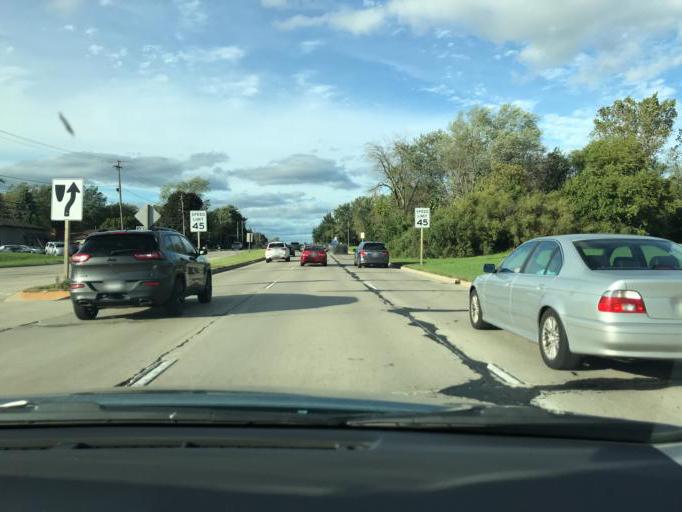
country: US
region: Wisconsin
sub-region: Kenosha County
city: Pleasant Prairie
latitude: 42.5830
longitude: -87.8837
